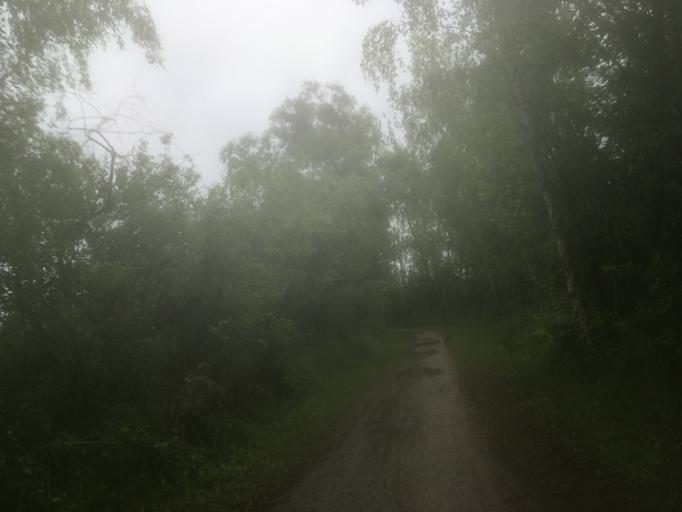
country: DE
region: Brandenburg
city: Zehdenick
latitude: 53.0217
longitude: 13.3096
